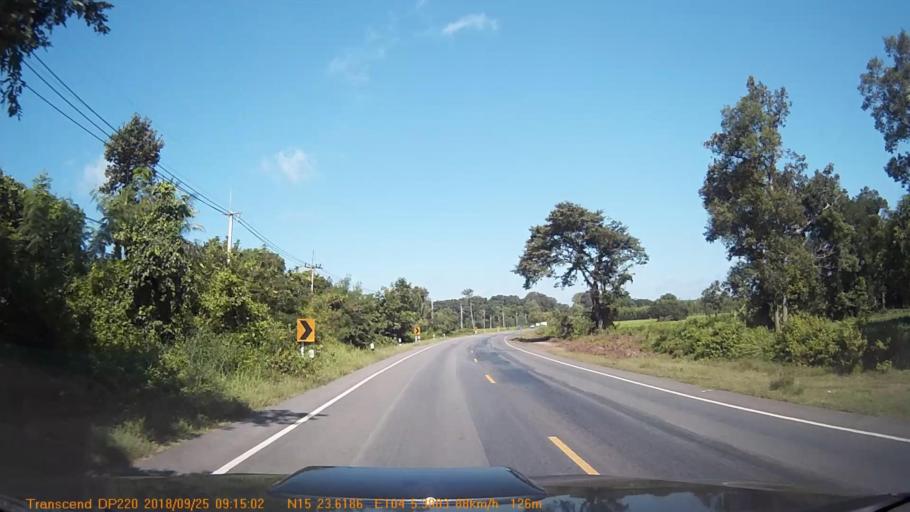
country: TH
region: Sisaket
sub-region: Amphoe Bueng Bun
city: Bueng Bun
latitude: 15.3936
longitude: 104.0898
